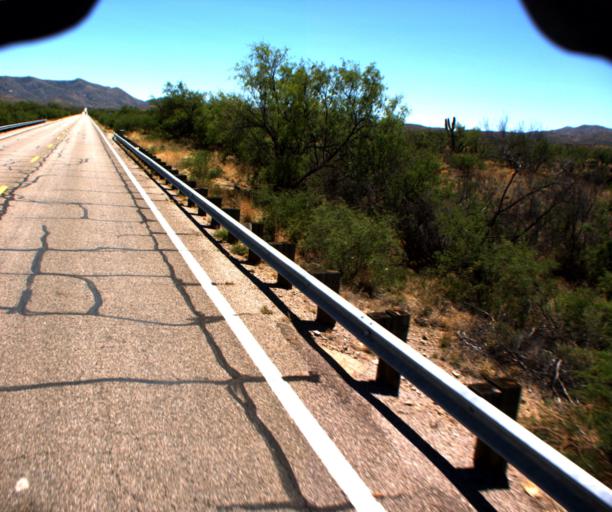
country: US
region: Arizona
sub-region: Pima County
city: Vail
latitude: 31.9606
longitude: -110.6710
